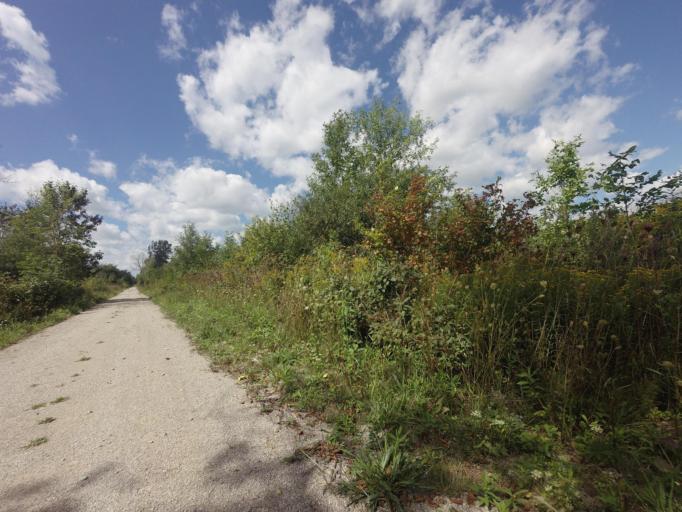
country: CA
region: Ontario
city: Huron East
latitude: 43.6201
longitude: -81.1536
